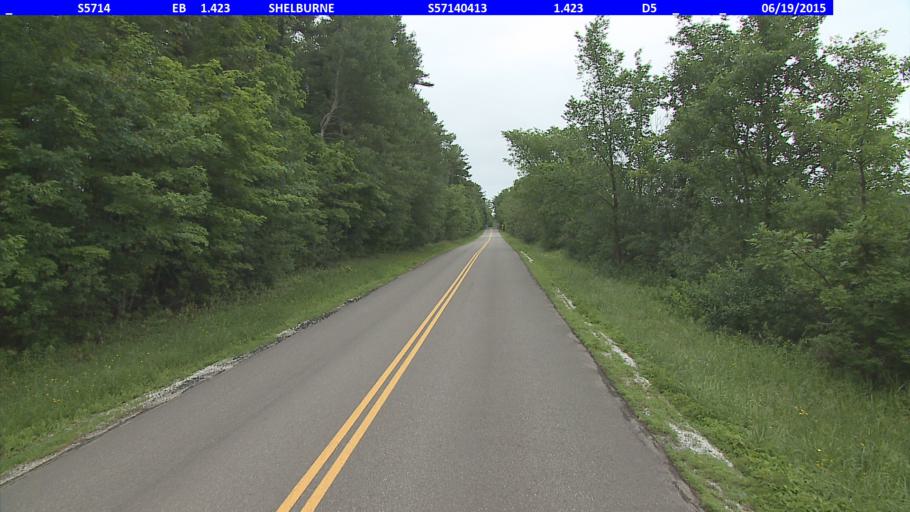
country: US
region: Vermont
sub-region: Chittenden County
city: Burlington
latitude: 44.3922
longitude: -73.2460
